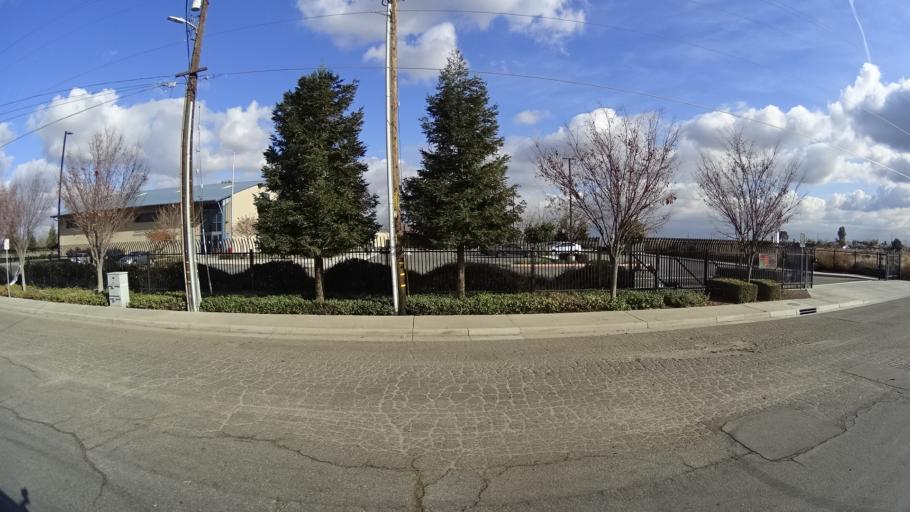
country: US
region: California
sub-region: Kern County
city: Bakersfield
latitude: 35.3278
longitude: -118.9855
